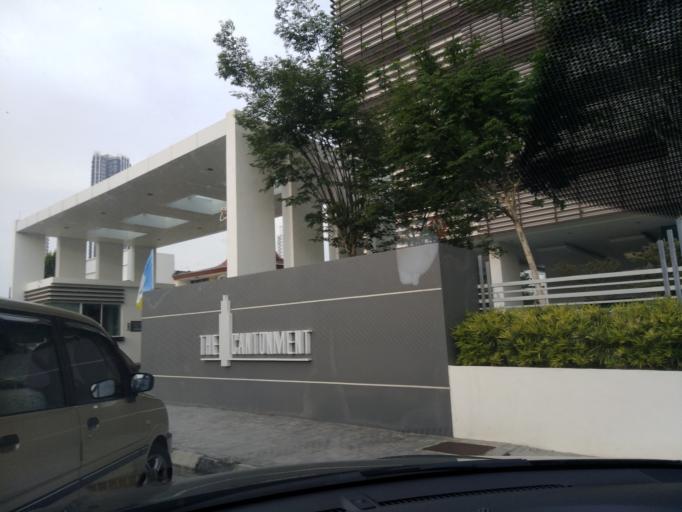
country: MY
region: Penang
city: George Town
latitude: 5.4301
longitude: 100.3112
